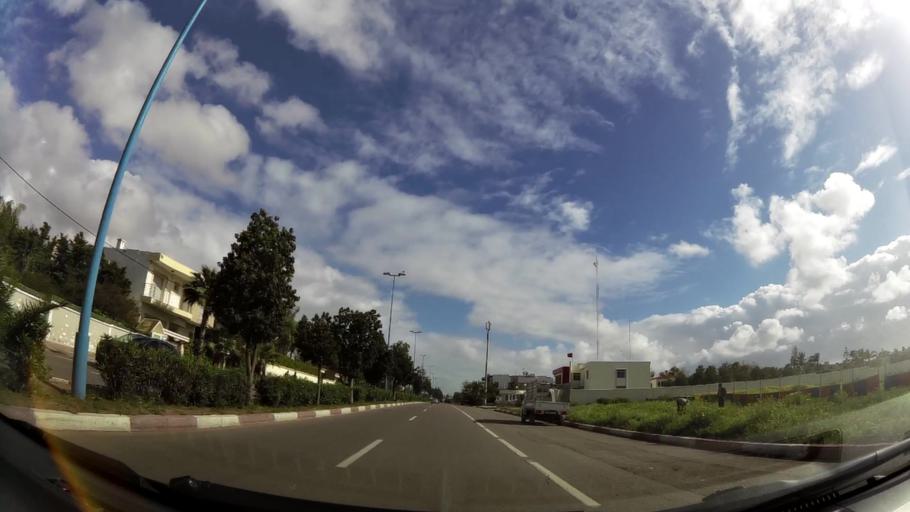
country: MA
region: Grand Casablanca
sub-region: Casablanca
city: Casablanca
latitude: 33.5486
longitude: -7.6224
